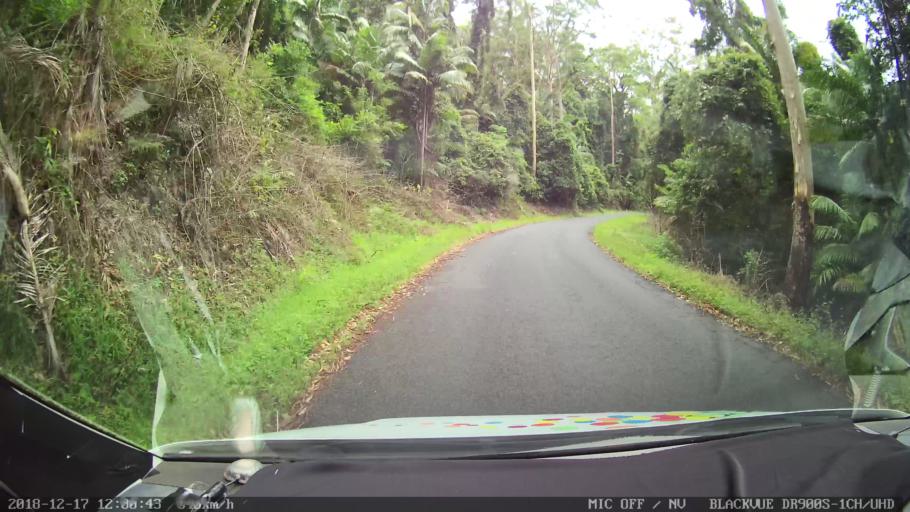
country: AU
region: New South Wales
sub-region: Kyogle
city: Kyogle
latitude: -28.5241
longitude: 152.5694
